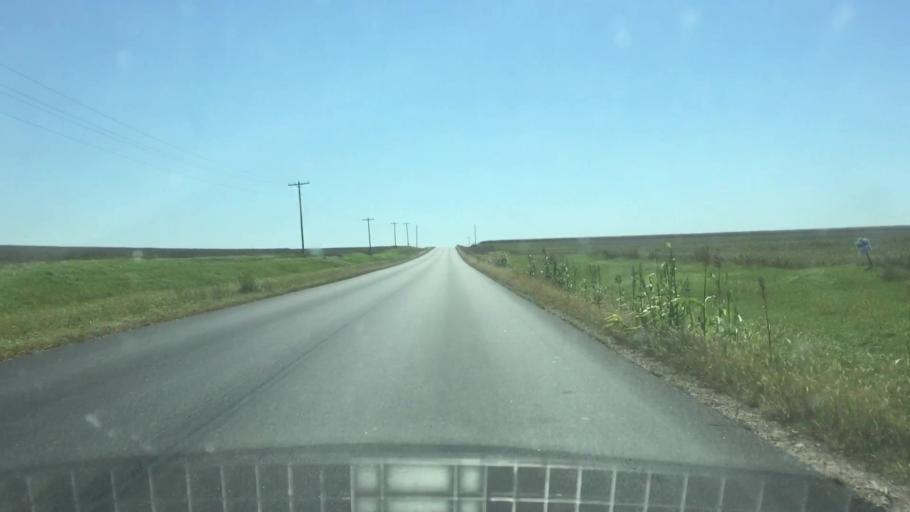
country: US
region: Kansas
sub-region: Marshall County
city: Marysville
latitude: 39.9113
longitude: -96.6010
